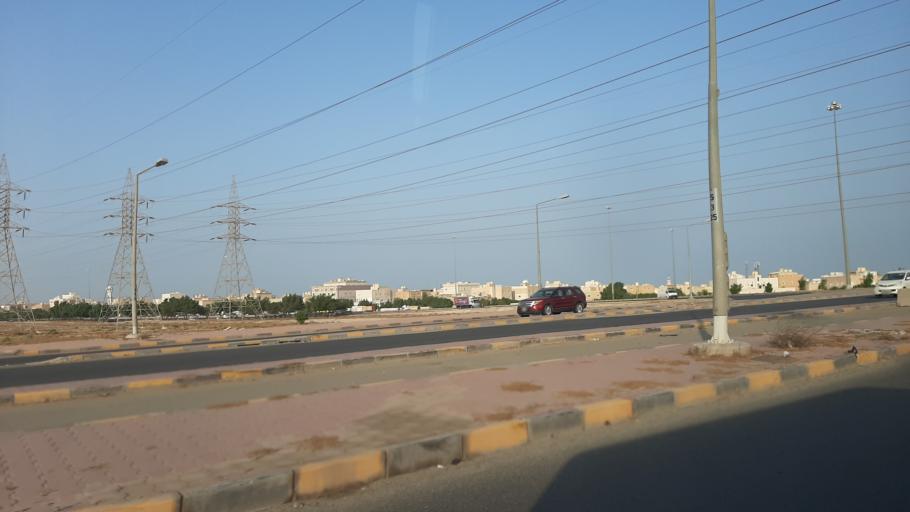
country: KW
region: Al Ahmadi
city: Al Ahmadi
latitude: 29.0937
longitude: 48.0955
